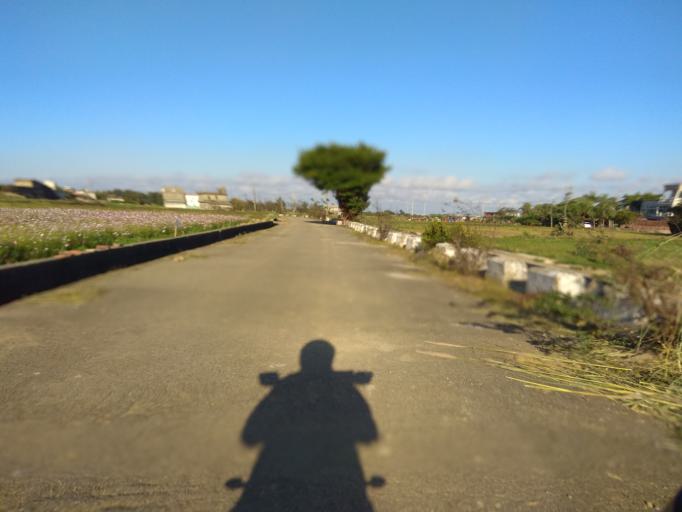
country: TW
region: Taiwan
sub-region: Hsinchu
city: Zhubei
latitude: 24.9862
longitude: 121.0534
